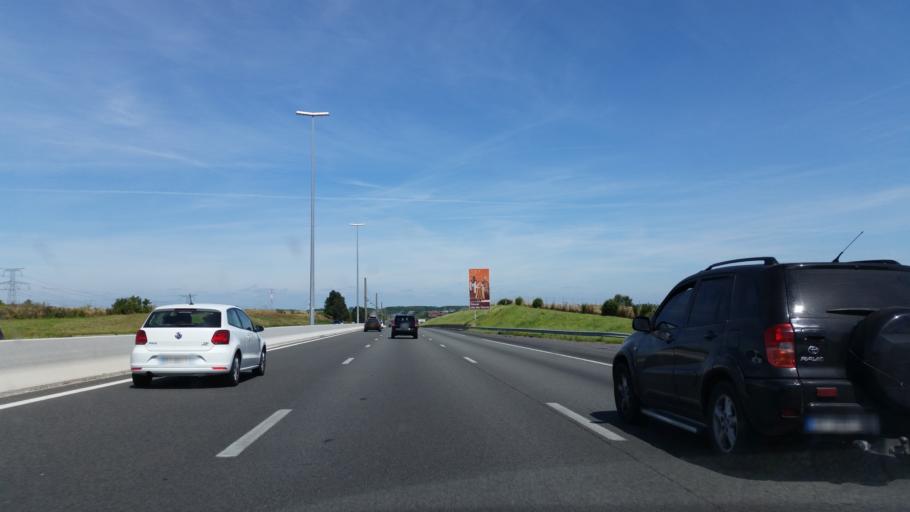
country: FR
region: Nord-Pas-de-Calais
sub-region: Departement du Pas-de-Calais
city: Fampoux
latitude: 50.2825
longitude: 2.8768
